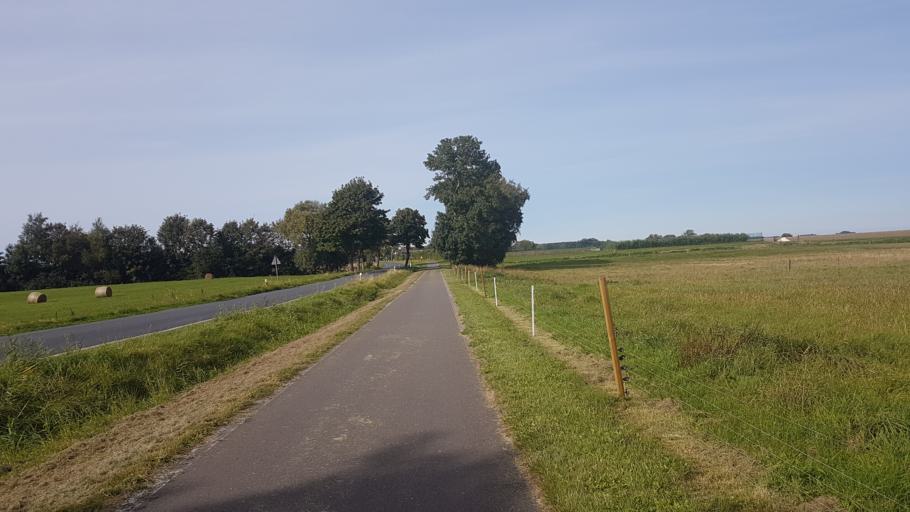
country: DE
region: Mecklenburg-Vorpommern
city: Gingst
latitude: 54.4484
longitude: 13.1855
